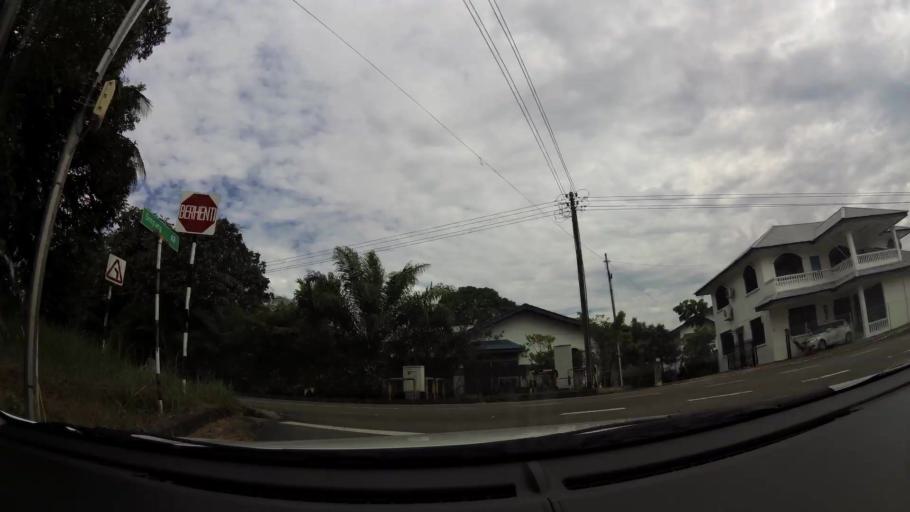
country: BN
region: Brunei and Muara
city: Bandar Seri Begawan
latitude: 4.8842
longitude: 114.9002
